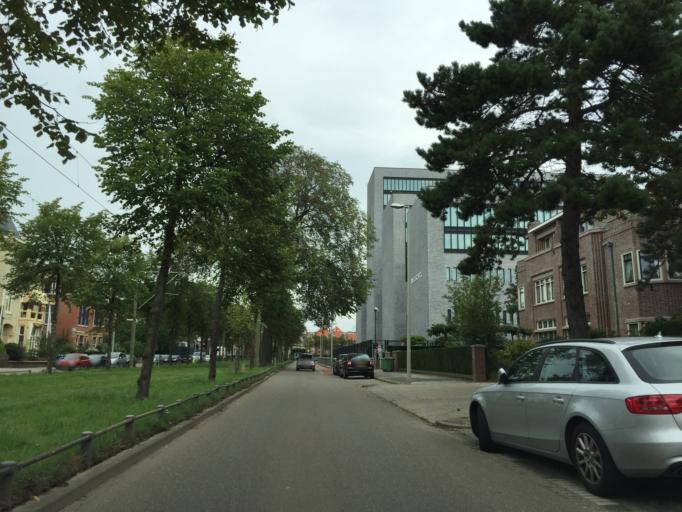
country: NL
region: South Holland
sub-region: Gemeente Den Haag
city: Scheveningen
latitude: 52.0919
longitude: 4.2800
